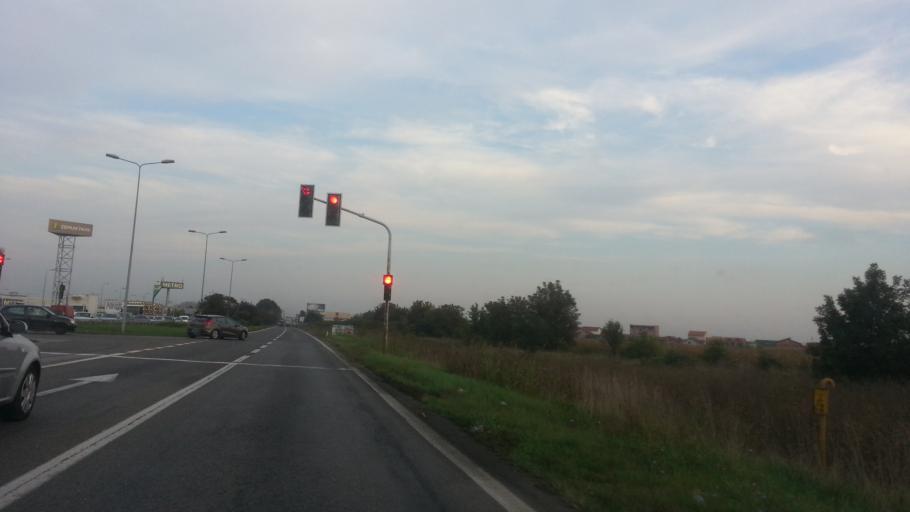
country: RS
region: Central Serbia
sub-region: Belgrade
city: Zemun
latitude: 44.8671
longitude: 20.3422
